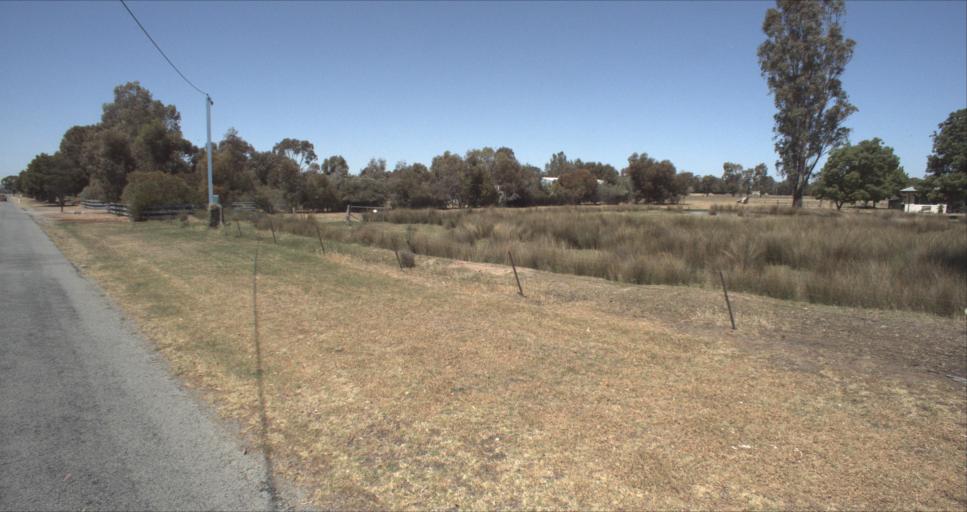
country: AU
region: New South Wales
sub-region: Leeton
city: Leeton
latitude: -34.5186
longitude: 146.4094
